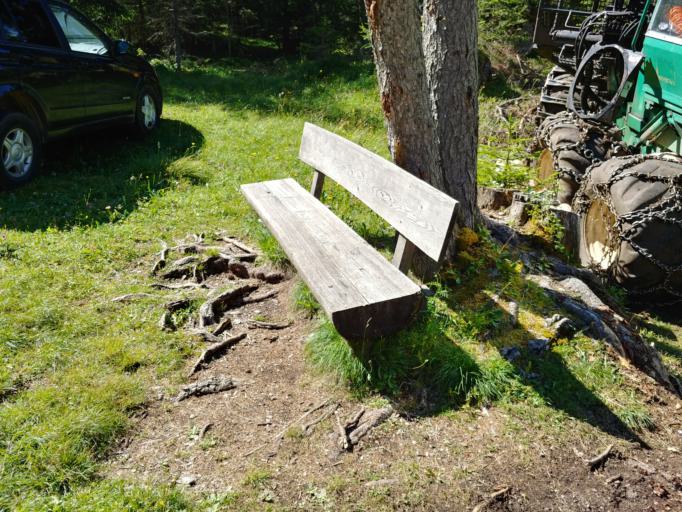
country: IT
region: Trentino-Alto Adige
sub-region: Bolzano
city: Santa Cristina Valgardena
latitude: 46.5365
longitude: 11.7042
